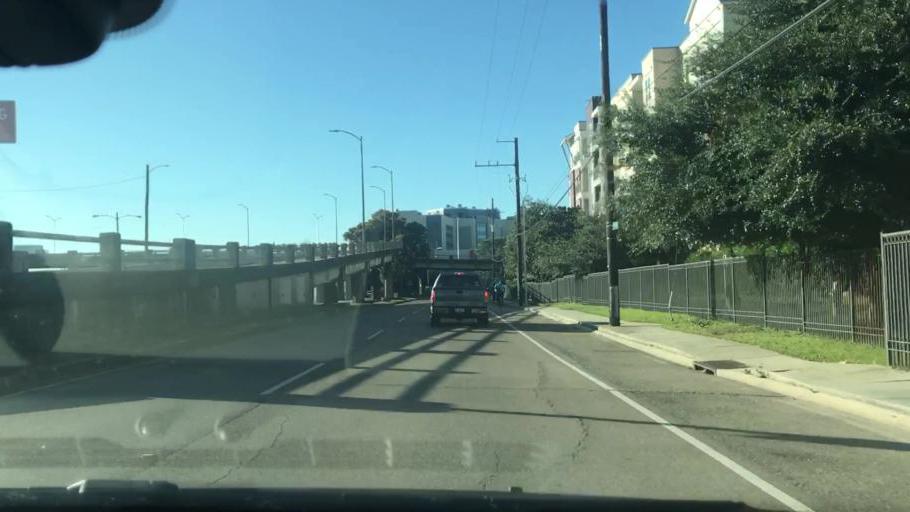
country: US
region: Louisiana
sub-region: Orleans Parish
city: New Orleans
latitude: 29.9582
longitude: -90.0917
